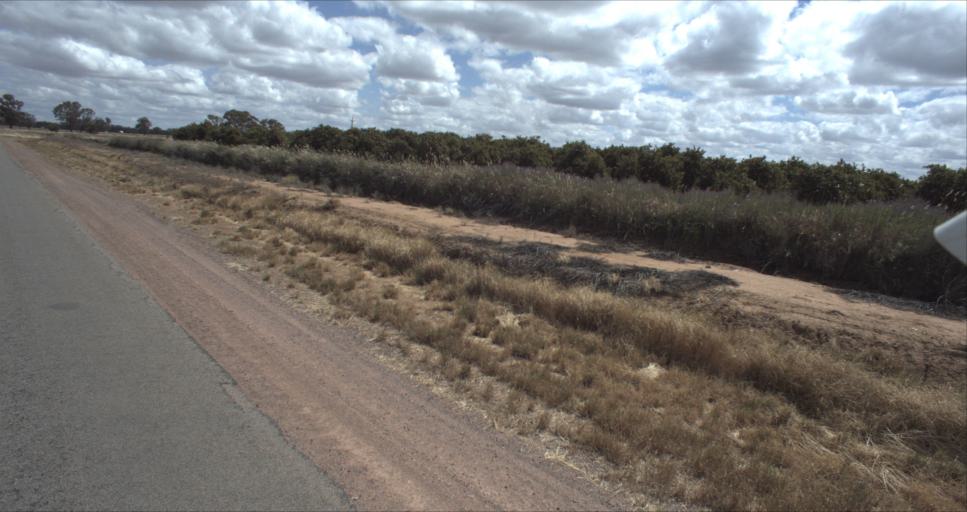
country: AU
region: New South Wales
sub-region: Leeton
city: Leeton
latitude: -34.5888
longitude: 146.3705
